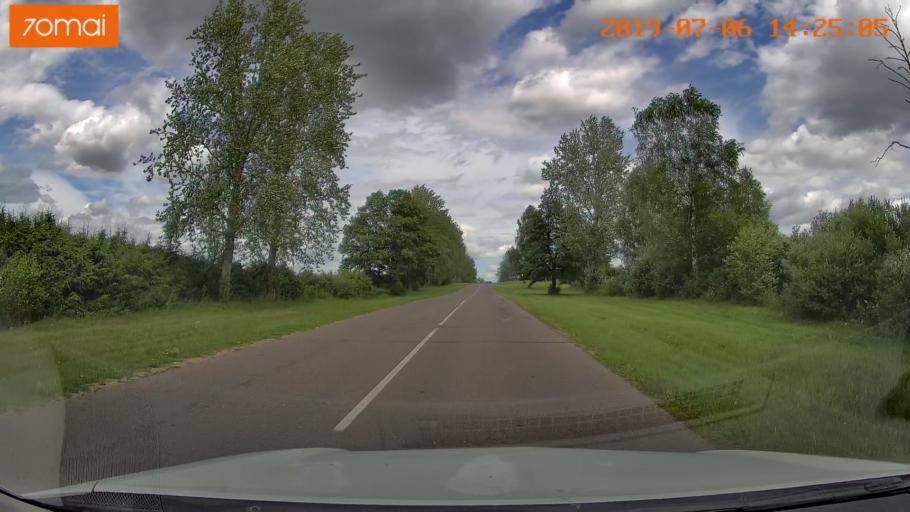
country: BY
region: Minsk
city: Ivyanyets
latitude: 53.9262
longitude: 26.7885
